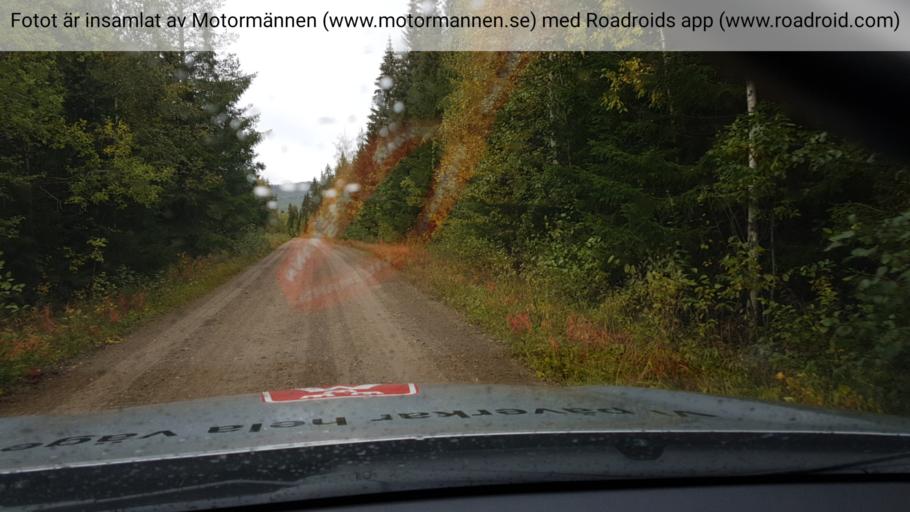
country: SE
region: Jaemtland
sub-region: Harjedalens Kommun
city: Sveg
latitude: 62.2452
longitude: 13.3059
